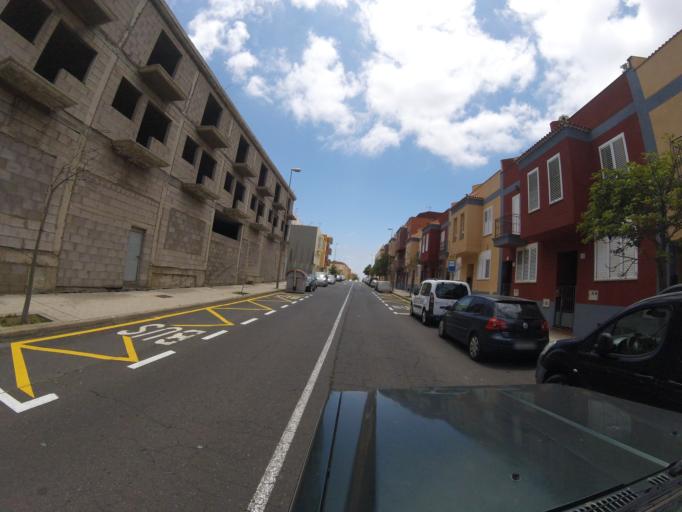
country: ES
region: Canary Islands
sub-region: Provincia de Santa Cruz de Tenerife
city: La Laguna
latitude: 28.4469
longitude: -16.3133
